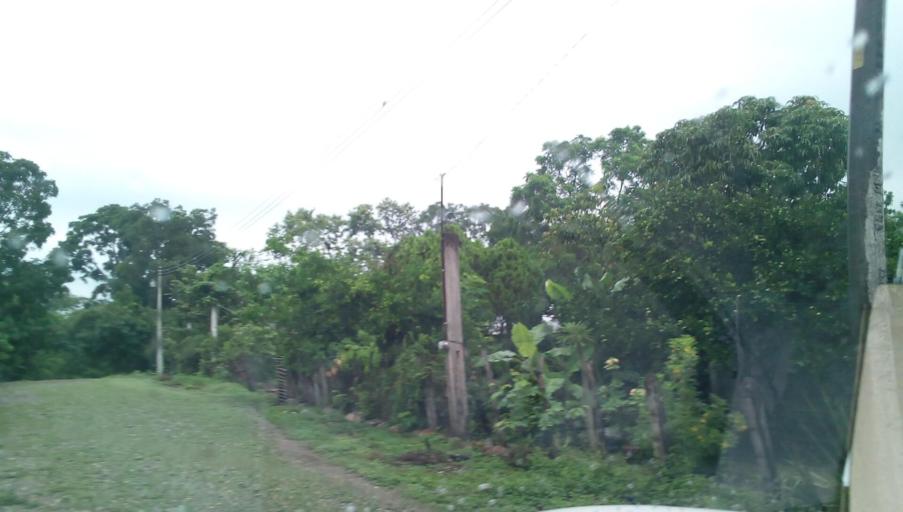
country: MX
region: Veracruz
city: Tempoal de Sanchez
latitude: 21.4203
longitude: -98.4255
